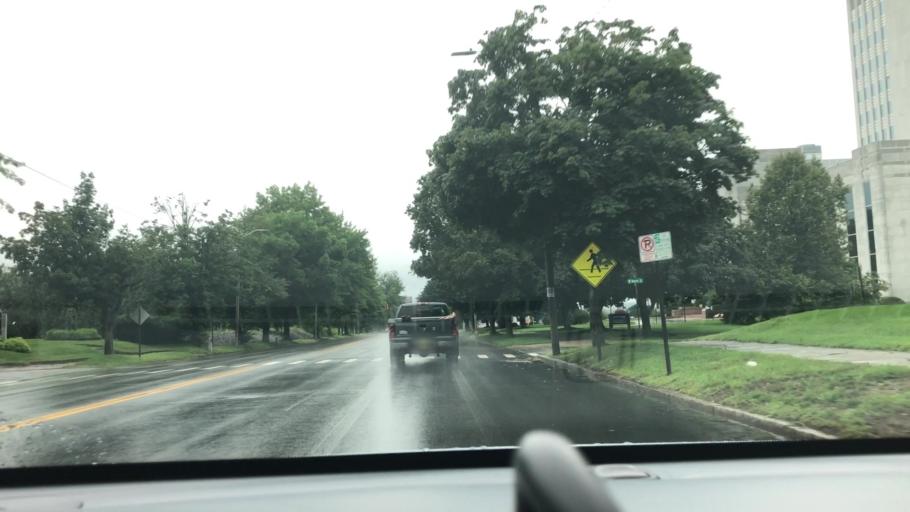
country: US
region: New Hampshire
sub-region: Hillsborough County
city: Manchester
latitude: 43.0048
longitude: -71.4652
